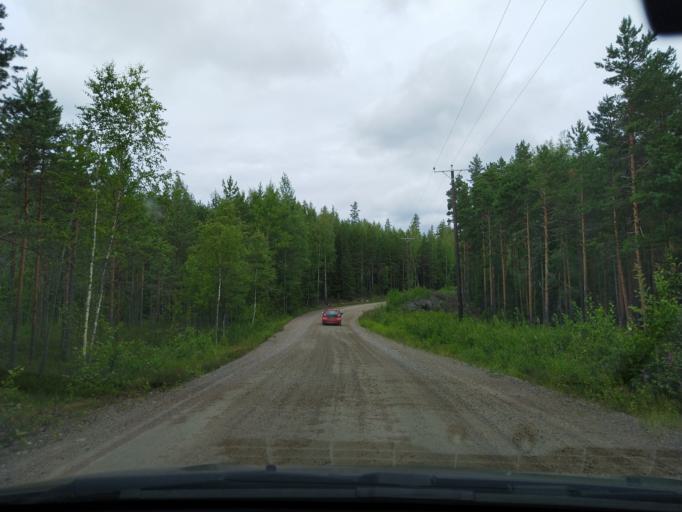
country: FI
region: Southern Savonia
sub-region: Mikkeli
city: Maentyharju
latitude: 61.1267
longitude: 26.8974
